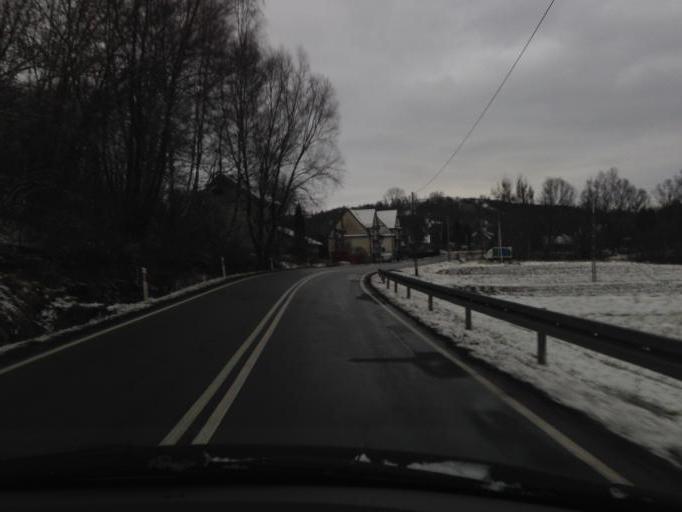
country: PL
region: Lesser Poland Voivodeship
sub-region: Powiat tarnowski
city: Gromnik
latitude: 49.8332
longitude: 20.9988
